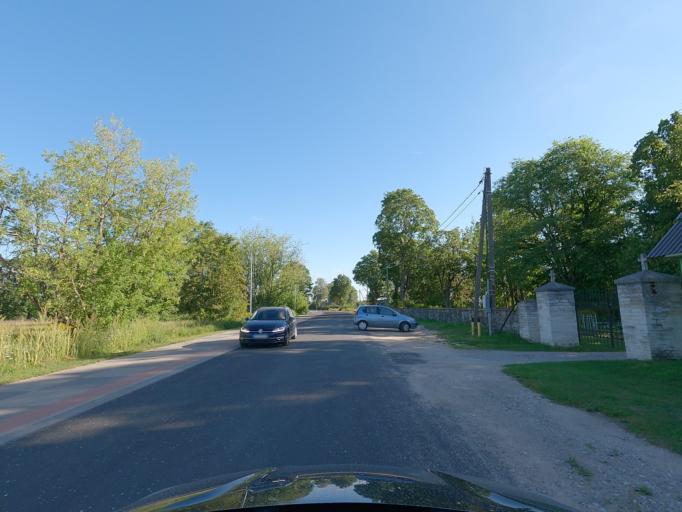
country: EE
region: Raplamaa
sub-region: Rapla vald
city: Rapla
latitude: 59.0132
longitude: 24.7851
